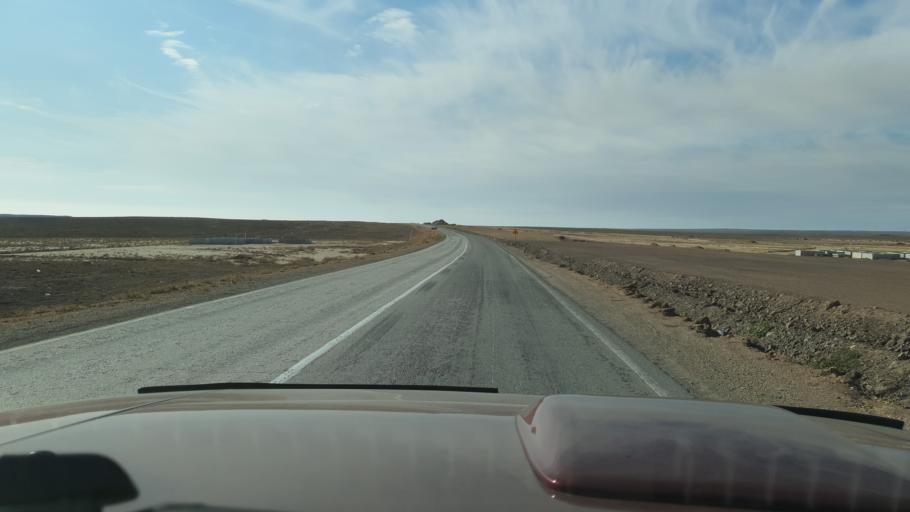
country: KZ
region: Qaraghandy
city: Saryshaghan
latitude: 46.3971
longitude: 73.8651
